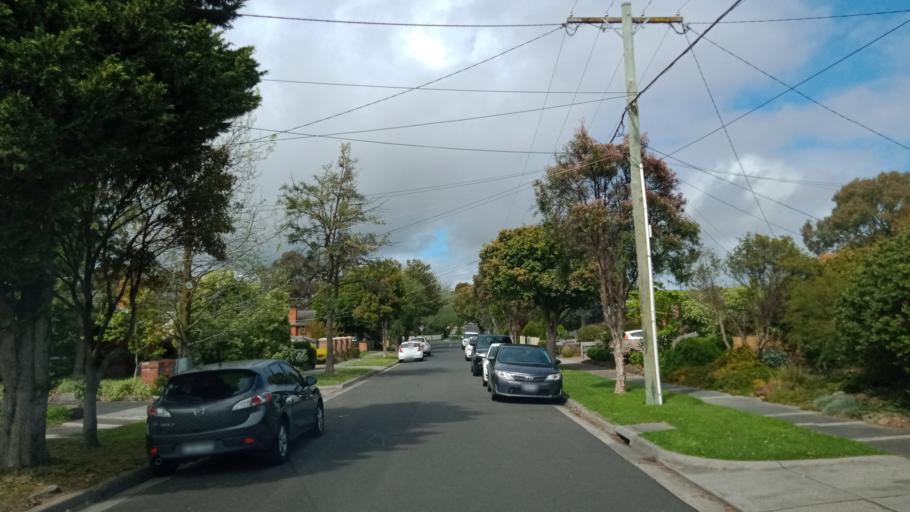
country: AU
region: Victoria
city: Burwood East
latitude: -37.8627
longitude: 145.1403
